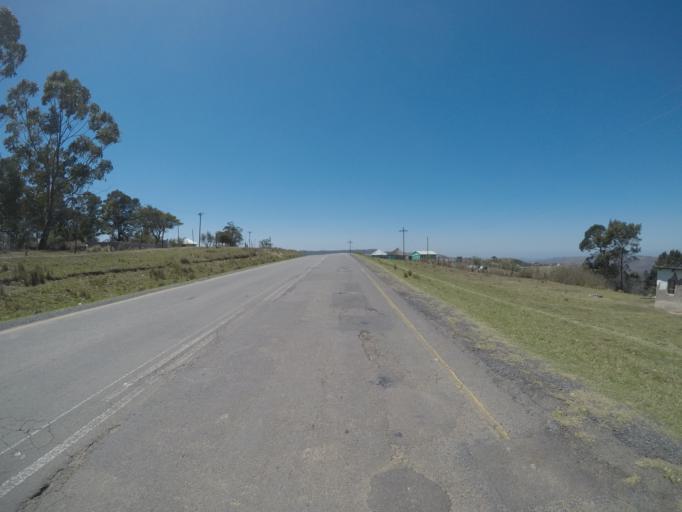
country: ZA
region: Eastern Cape
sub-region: OR Tambo District Municipality
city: Mthatha
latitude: -31.8977
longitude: 28.9374
